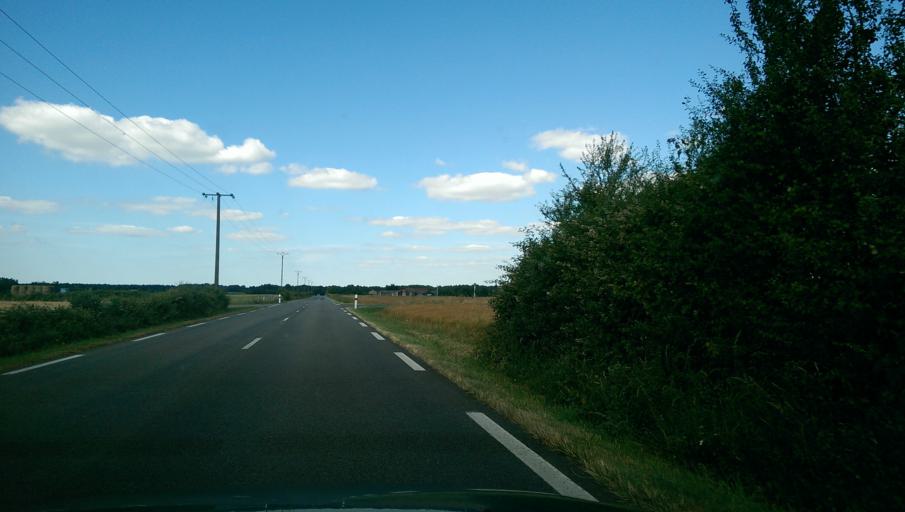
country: FR
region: Pays de la Loire
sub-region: Departement de la Vendee
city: Rocheserviere
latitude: 46.9131
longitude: -1.5499
